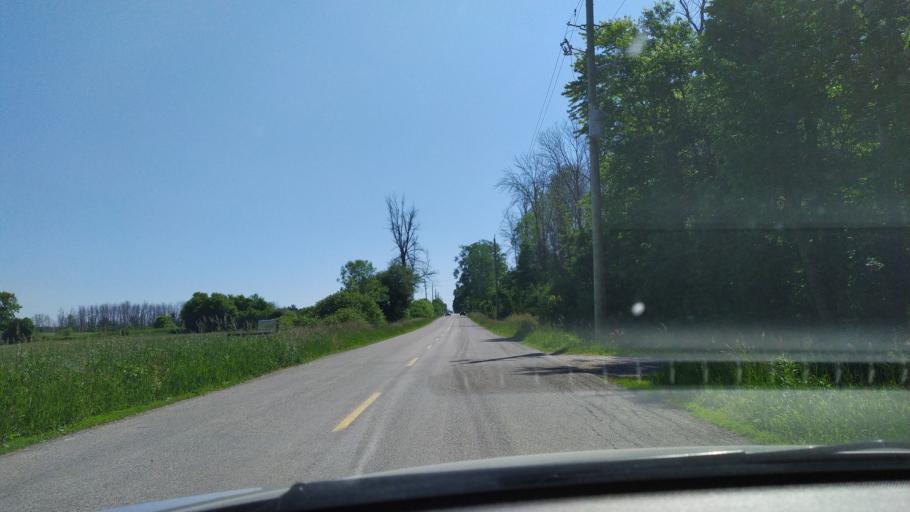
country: CA
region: Ontario
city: Waterloo
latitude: 43.4682
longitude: -80.6562
